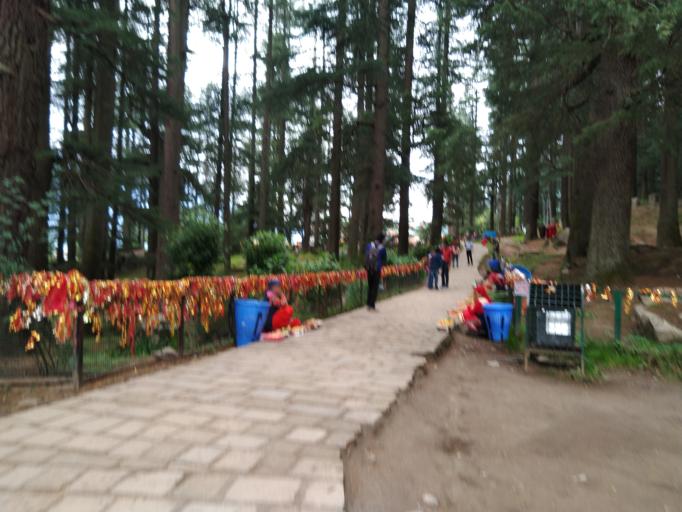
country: IN
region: Himachal Pradesh
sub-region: Kulu
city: Manali
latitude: 32.2481
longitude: 77.1808
